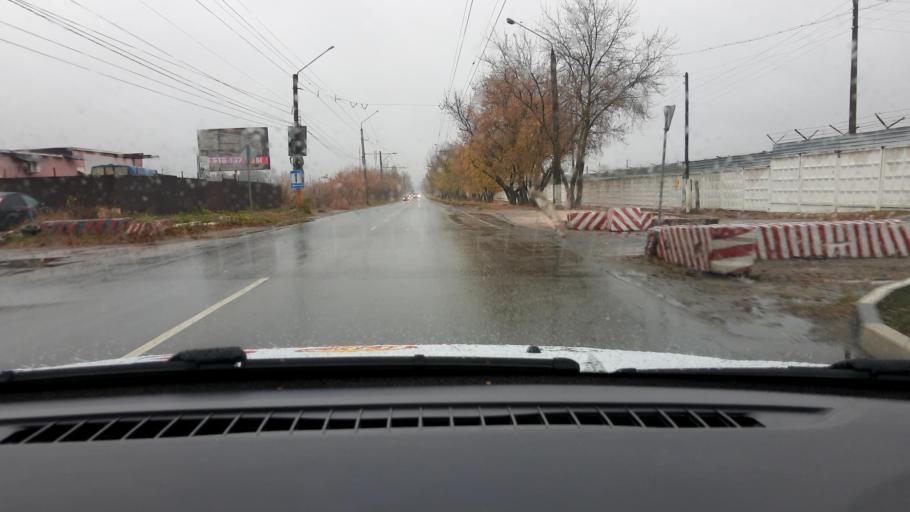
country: RU
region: Nizjnij Novgorod
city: Dzerzhinsk
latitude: 56.2461
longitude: 43.4814
